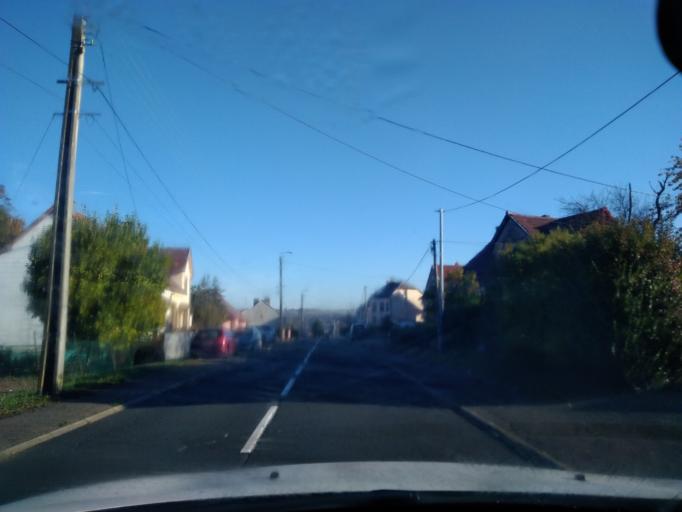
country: FR
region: Lorraine
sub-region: Departement de la Moselle
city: Sarreguemines
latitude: 49.1086
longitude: 7.0455
